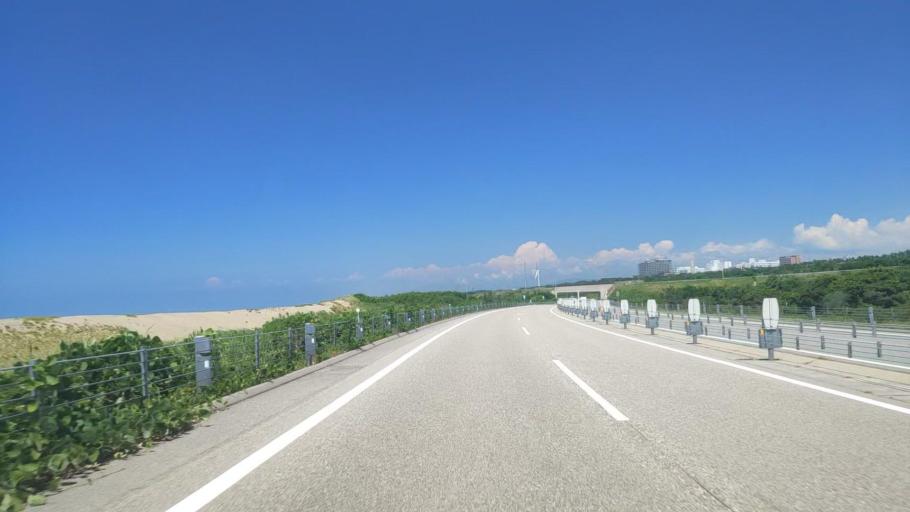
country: JP
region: Ishikawa
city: Kanazawa-shi
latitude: 36.6490
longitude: 136.6315
